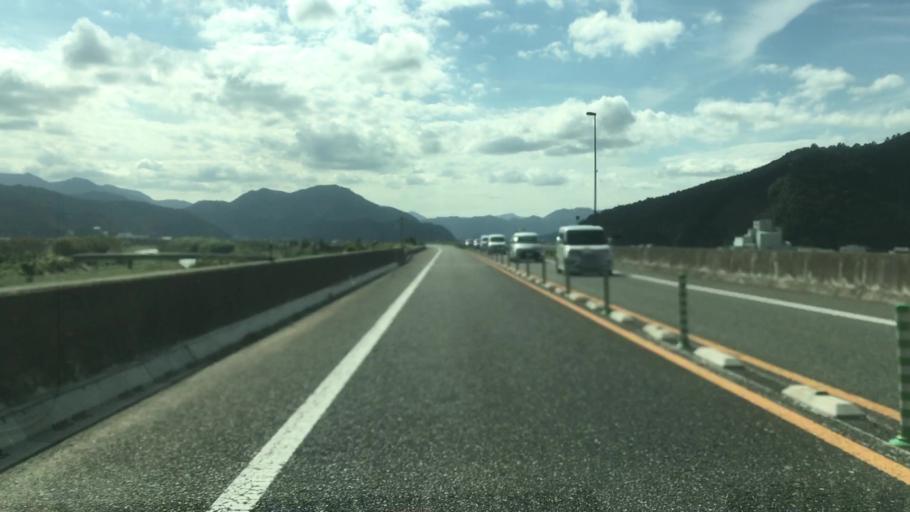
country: JP
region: Kyoto
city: Fukuchiyama
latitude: 35.2130
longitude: 135.0362
